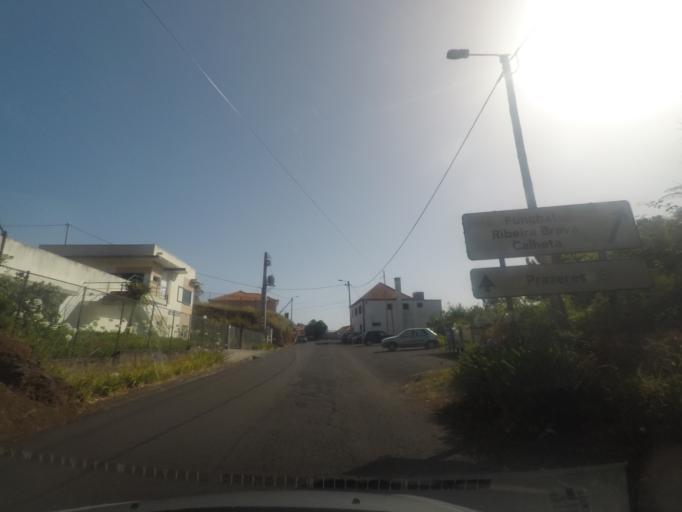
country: PT
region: Madeira
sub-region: Calheta
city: Estreito da Calheta
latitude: 32.7580
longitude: -17.2010
